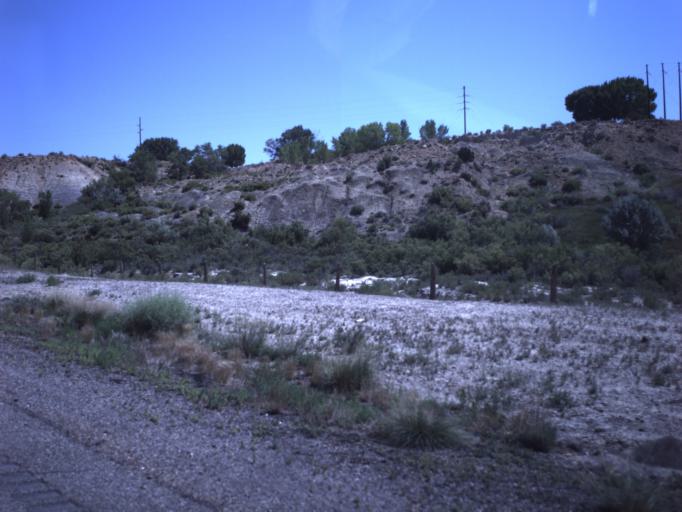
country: US
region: Utah
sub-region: Emery County
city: Ferron
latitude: 38.8881
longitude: -111.2830
